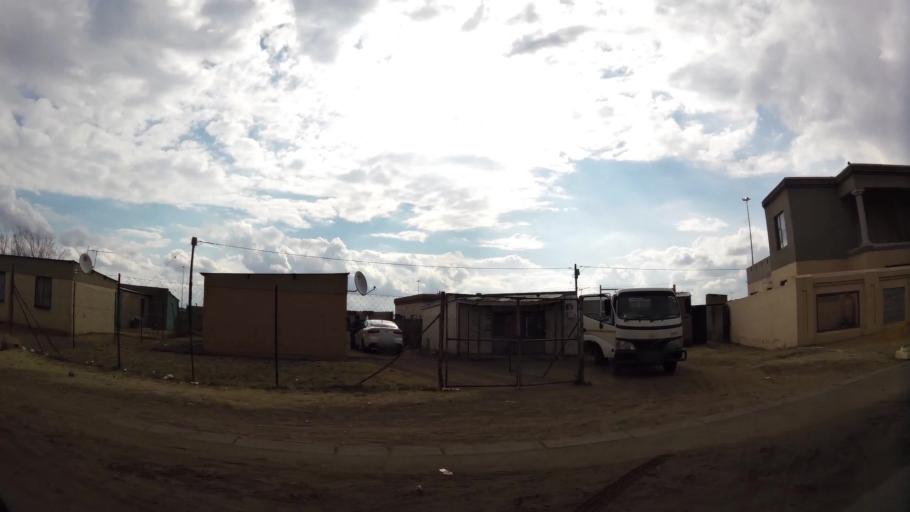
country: ZA
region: Gauteng
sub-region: Sedibeng District Municipality
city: Vanderbijlpark
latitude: -26.6847
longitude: 27.7798
